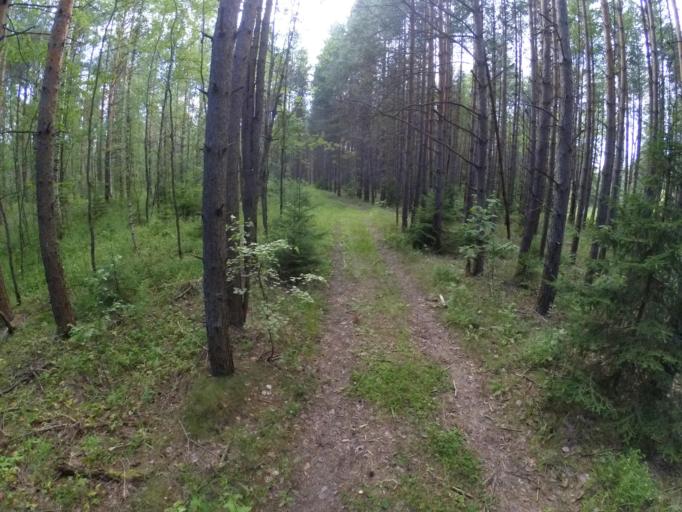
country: RU
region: Moskovskaya
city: Fosforitnyy
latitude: 55.3329
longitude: 38.9350
